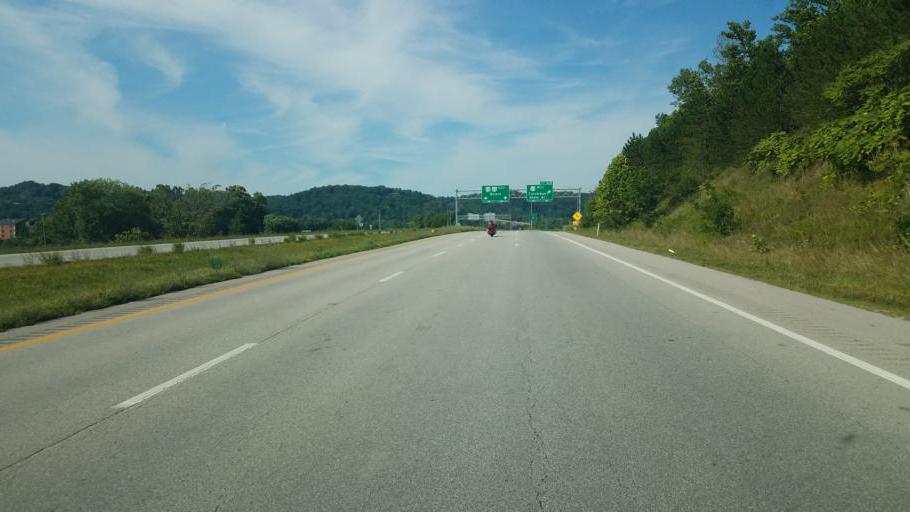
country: US
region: Ohio
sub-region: Athens County
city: Athens
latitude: 39.3262
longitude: -82.0875
